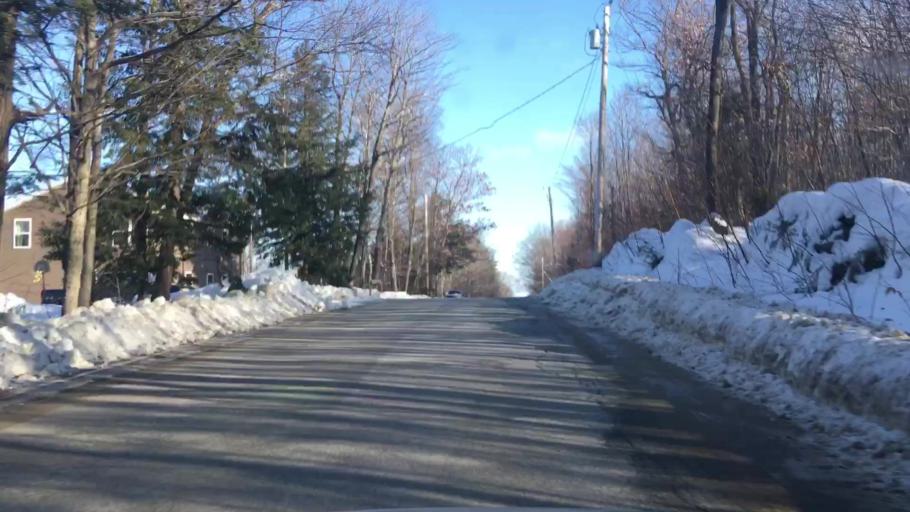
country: US
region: Maine
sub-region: Oxford County
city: Paris
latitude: 44.2724
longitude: -70.4432
